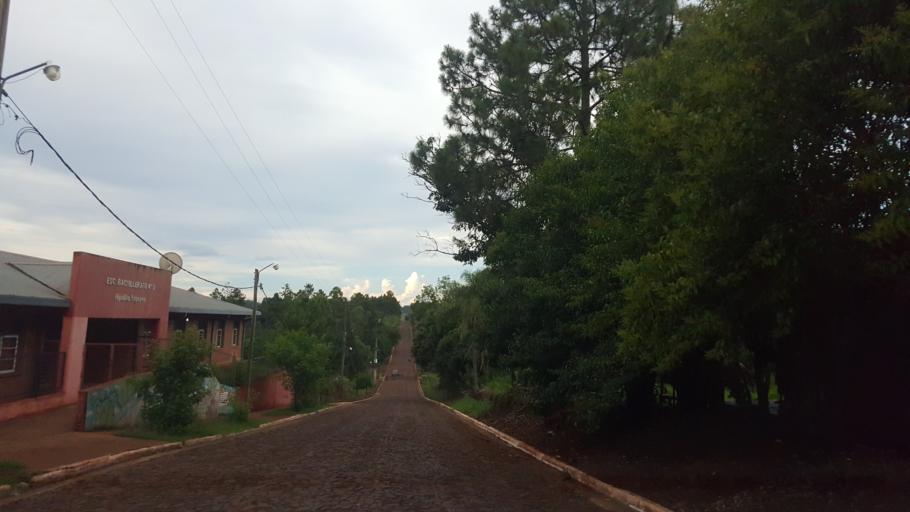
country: AR
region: Misiones
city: Jardin America
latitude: -27.0827
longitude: -55.2864
